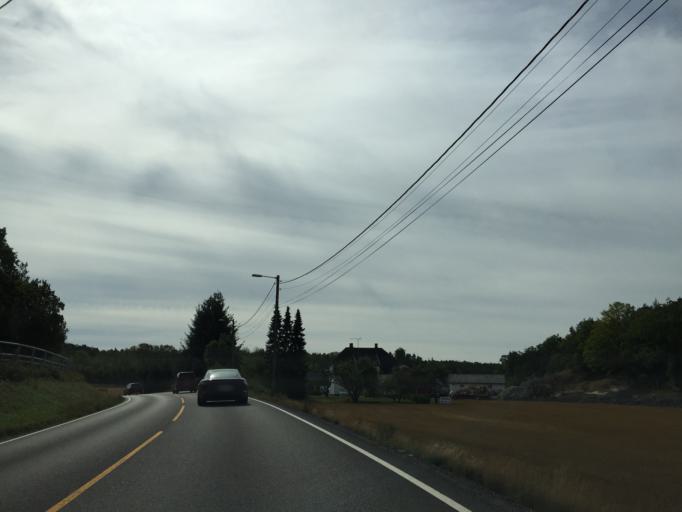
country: NO
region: Ostfold
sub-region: Fredrikstad
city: Fredrikstad
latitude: 59.1630
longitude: 10.9282
